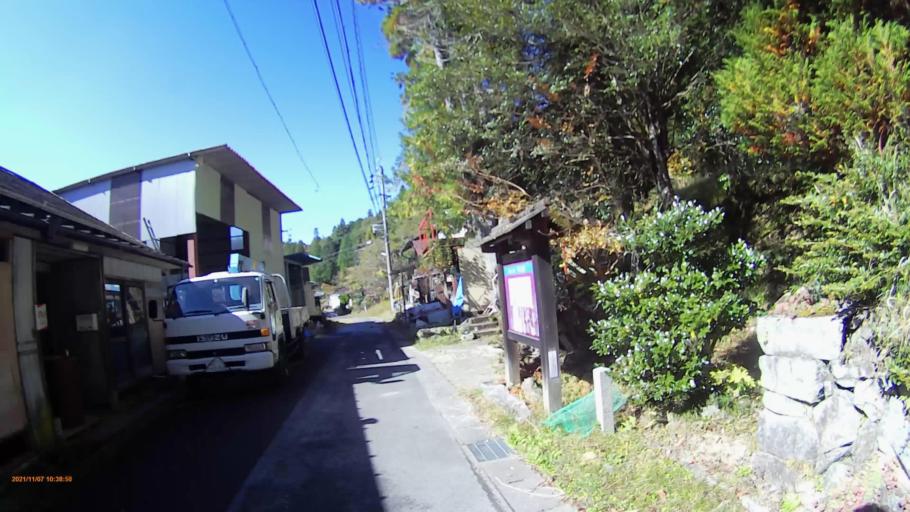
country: JP
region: Gifu
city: Mizunami
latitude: 35.4393
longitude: 137.3191
